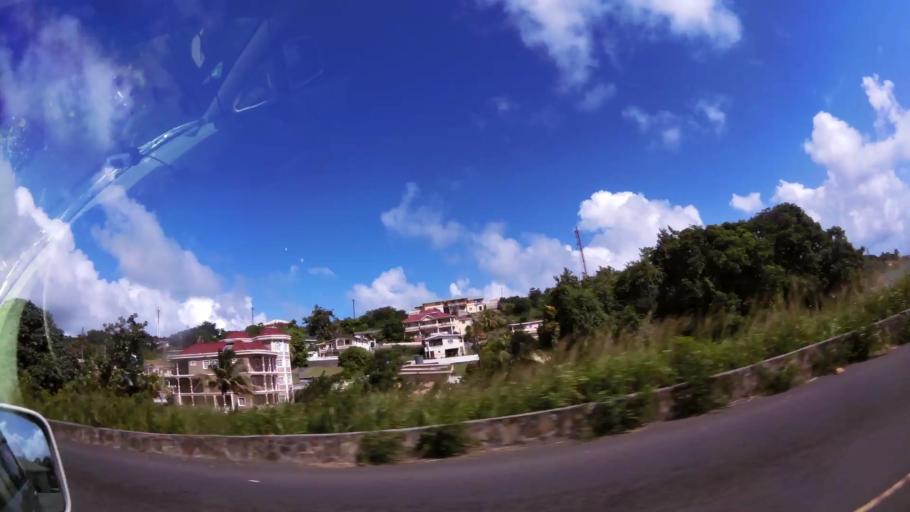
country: VC
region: Saint George
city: Kingstown
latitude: 13.1313
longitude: -61.1848
